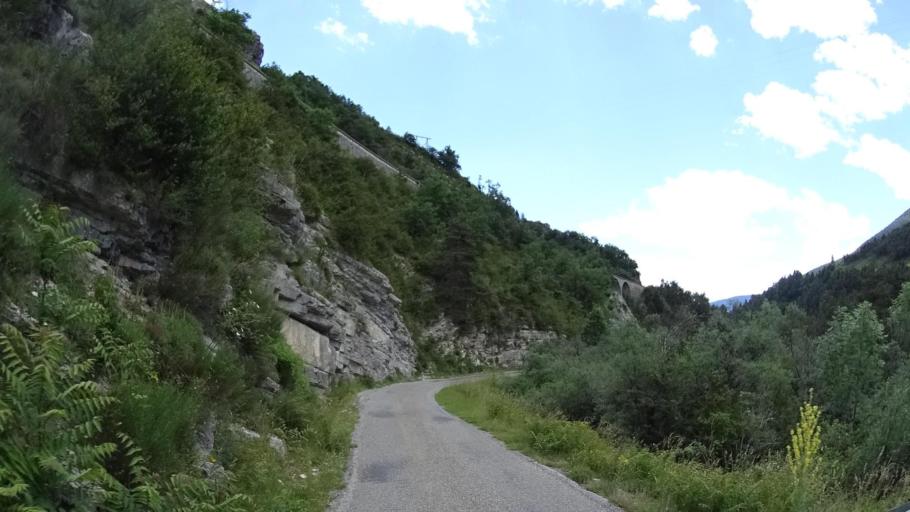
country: FR
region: Provence-Alpes-Cote d'Azur
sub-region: Departement des Alpes-de-Haute-Provence
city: Annot
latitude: 44.0225
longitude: 6.6289
